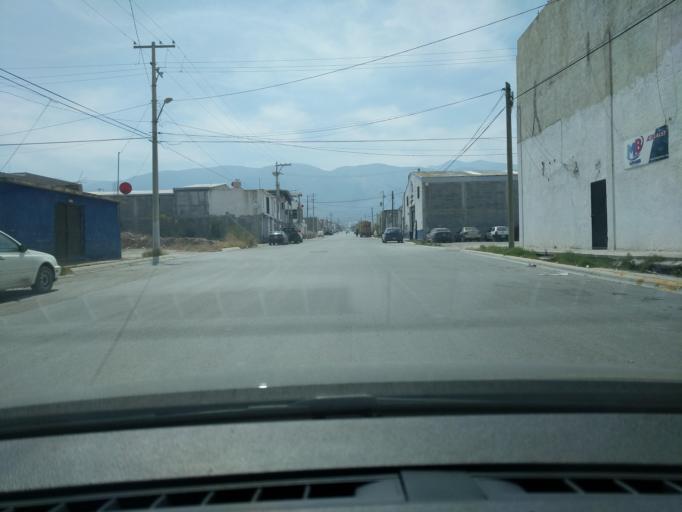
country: MX
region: Coahuila
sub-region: Arteaga
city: Arteaga
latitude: 25.4333
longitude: -100.9106
